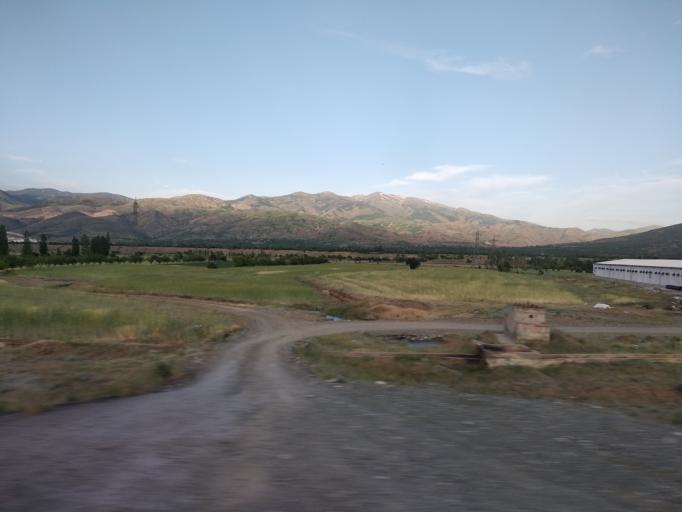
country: TR
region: Erzincan
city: Catalarmut
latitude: 39.8190
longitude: 39.3513
